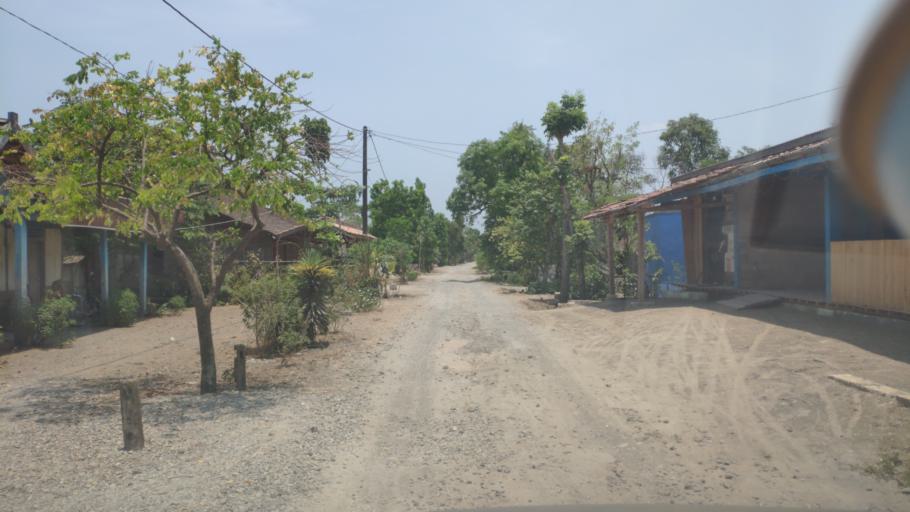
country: ID
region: Central Java
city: Temulus
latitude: -7.2262
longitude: 111.4272
